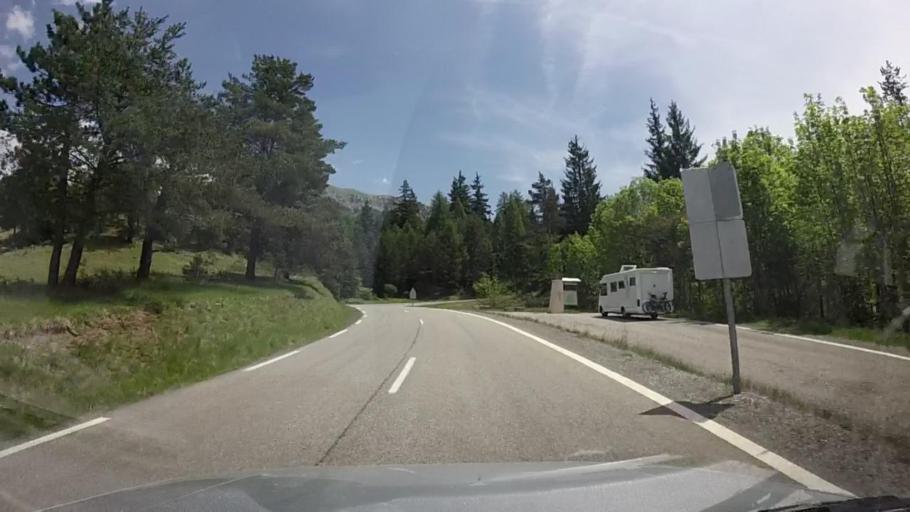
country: FR
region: Provence-Alpes-Cote d'Azur
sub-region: Departement des Alpes-de-Haute-Provence
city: Seyne-les-Alpes
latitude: 44.2516
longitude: 6.3715
